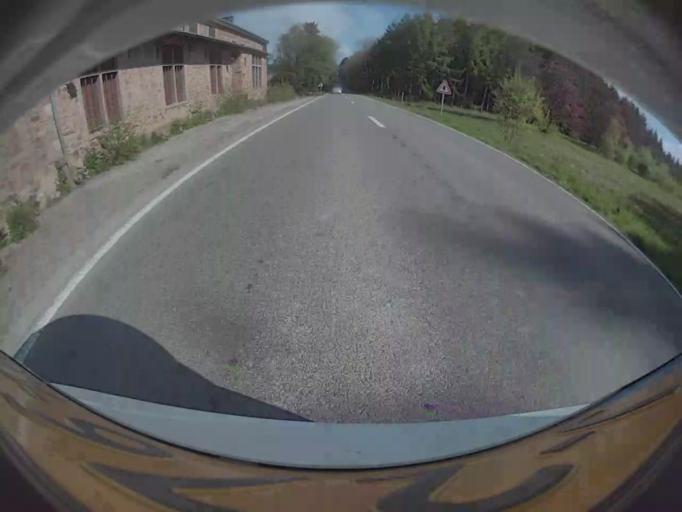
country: BE
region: Wallonia
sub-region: Province du Luxembourg
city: Tellin
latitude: 50.0304
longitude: 5.2068
